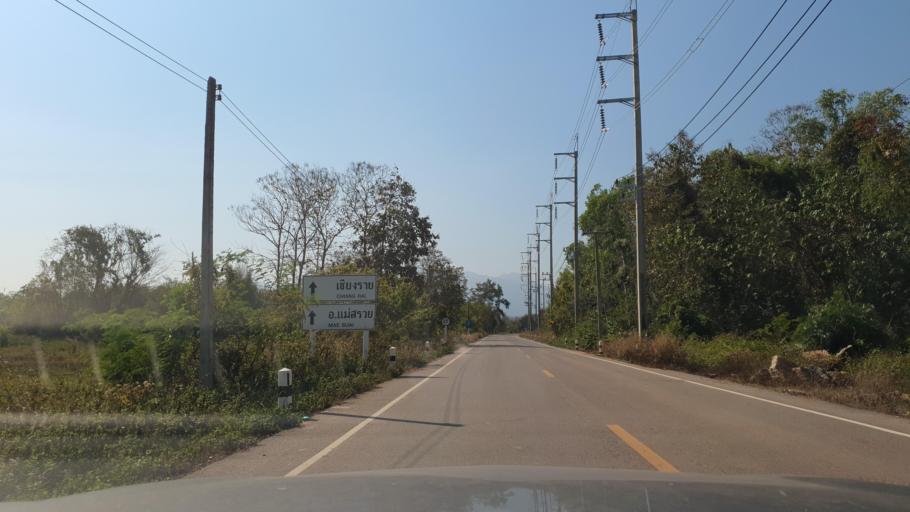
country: TH
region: Chiang Rai
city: Mae Lao
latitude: 19.7993
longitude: 99.6997
